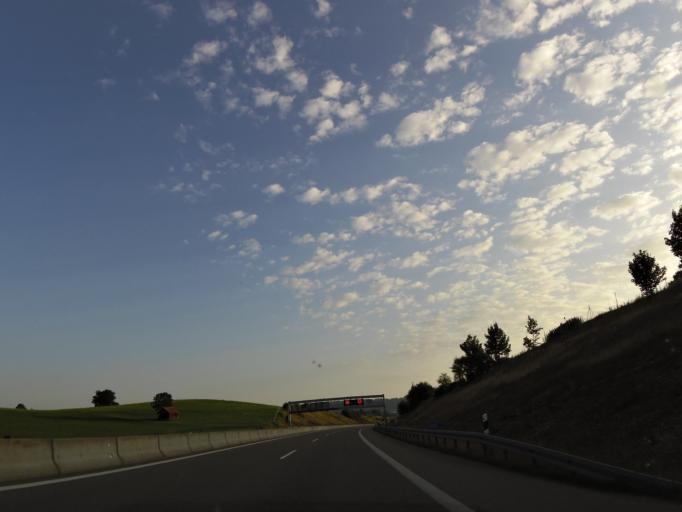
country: DE
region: Bavaria
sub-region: Swabia
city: Hopferau
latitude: 47.5921
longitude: 10.6565
